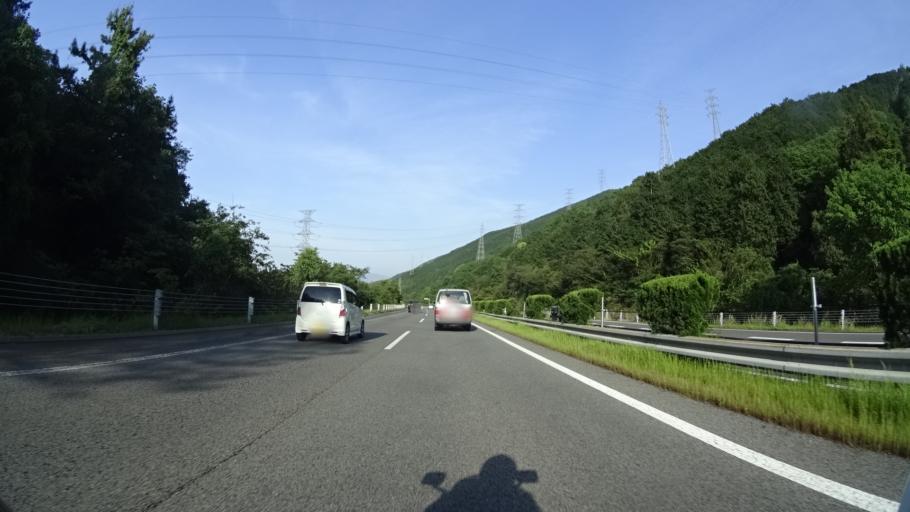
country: JP
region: Ehime
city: Niihama
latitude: 33.9418
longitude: 133.3957
